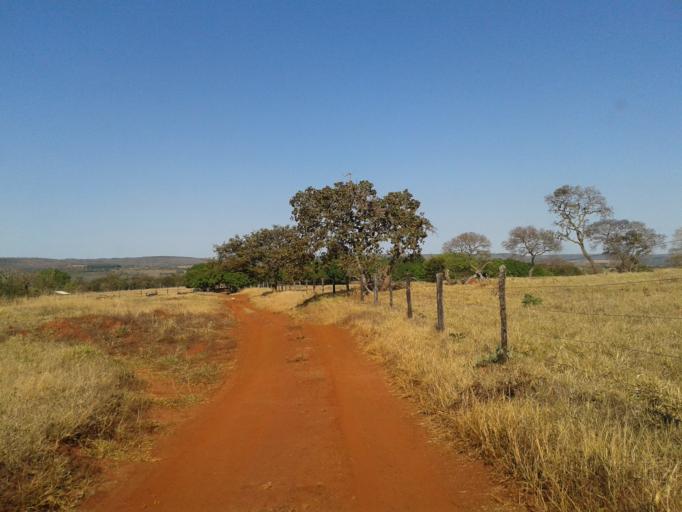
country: BR
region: Minas Gerais
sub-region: Ituiutaba
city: Ituiutaba
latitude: -19.0486
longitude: -49.2883
